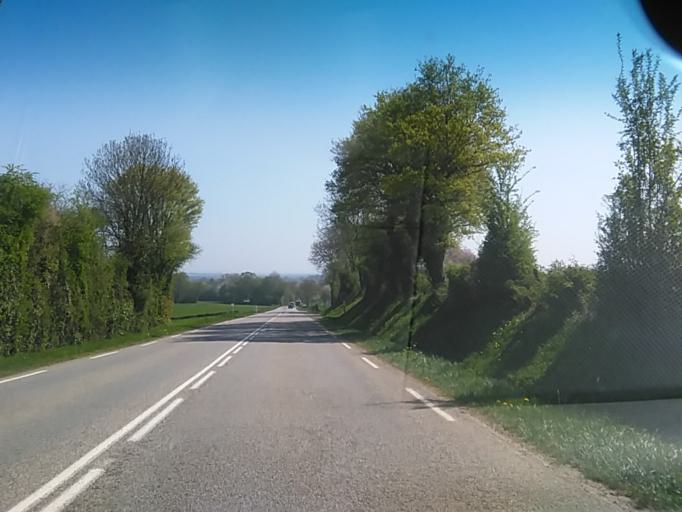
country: FR
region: Lower Normandy
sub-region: Departement de l'Orne
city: Courteilles
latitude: 48.7125
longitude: -0.1949
